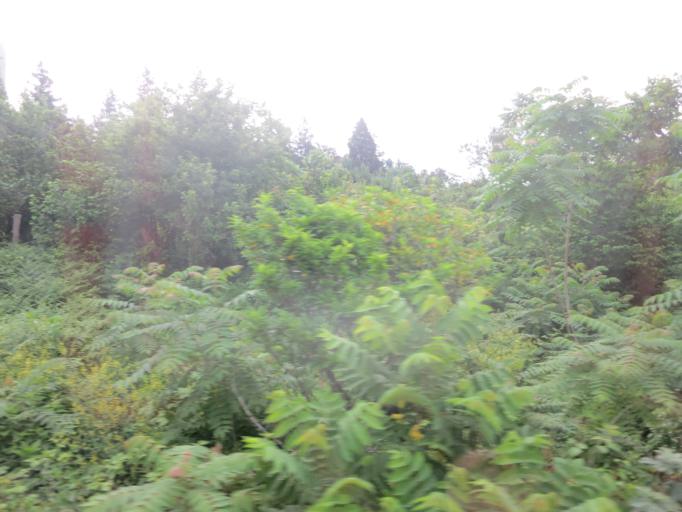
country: GE
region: Ajaria
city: Makhinjauri
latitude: 41.7412
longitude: 41.7358
